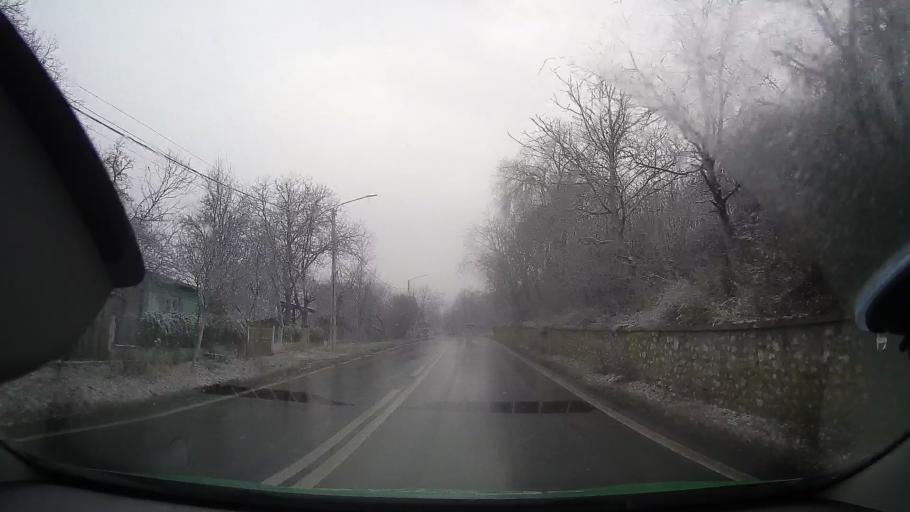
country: RO
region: Mures
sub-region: Comuna Bagaciu
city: Delenii
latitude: 46.2694
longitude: 24.2995
